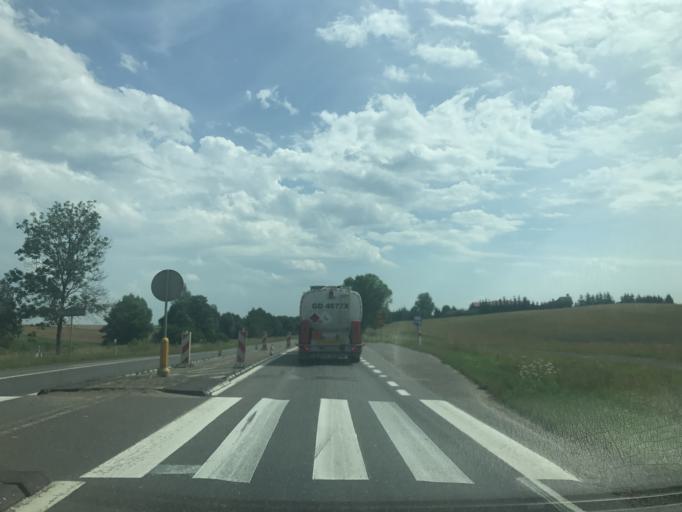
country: PL
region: Warmian-Masurian Voivodeship
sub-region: Powiat ostrodzki
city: Ostroda
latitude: 53.6718
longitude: 20.0335
